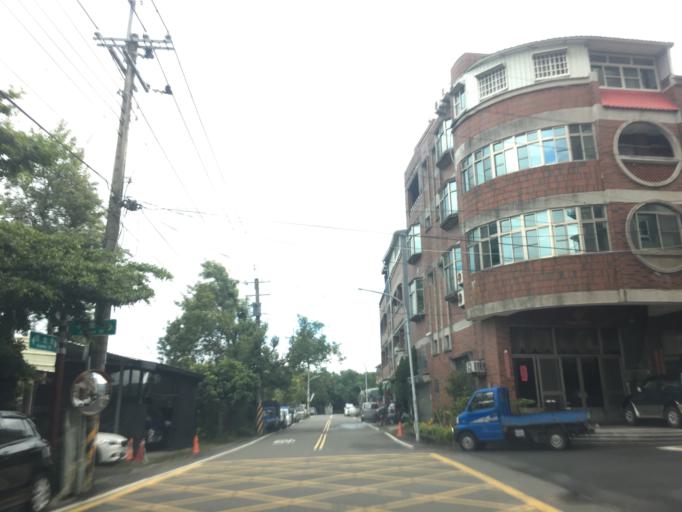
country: TW
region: Taiwan
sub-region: Yunlin
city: Douliu
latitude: 23.5891
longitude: 120.5502
